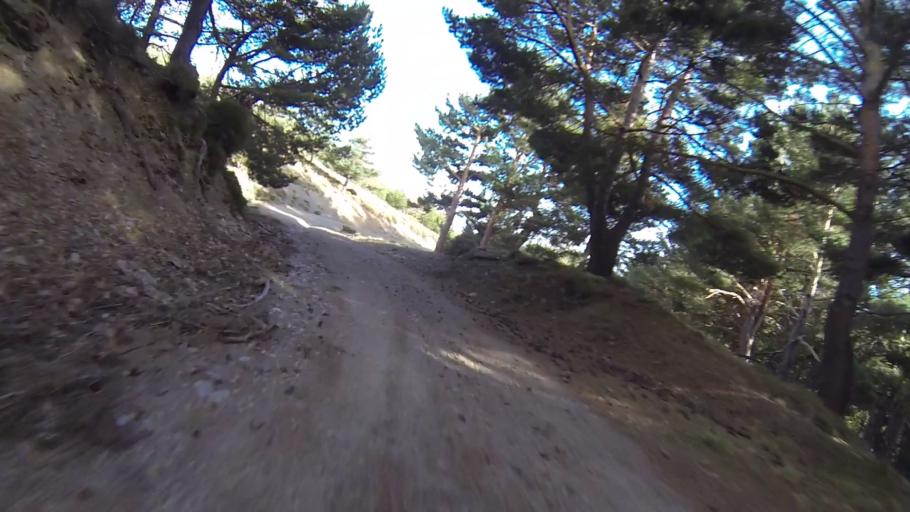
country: ES
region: Andalusia
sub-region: Provincia de Almeria
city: Paterna del Rio
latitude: 37.0833
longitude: -2.9035
